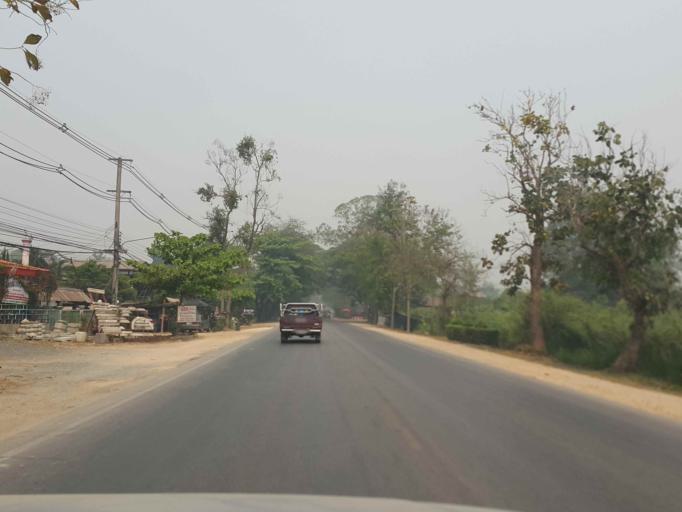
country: TH
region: Chiang Mai
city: San Sai
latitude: 18.9330
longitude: 98.9888
